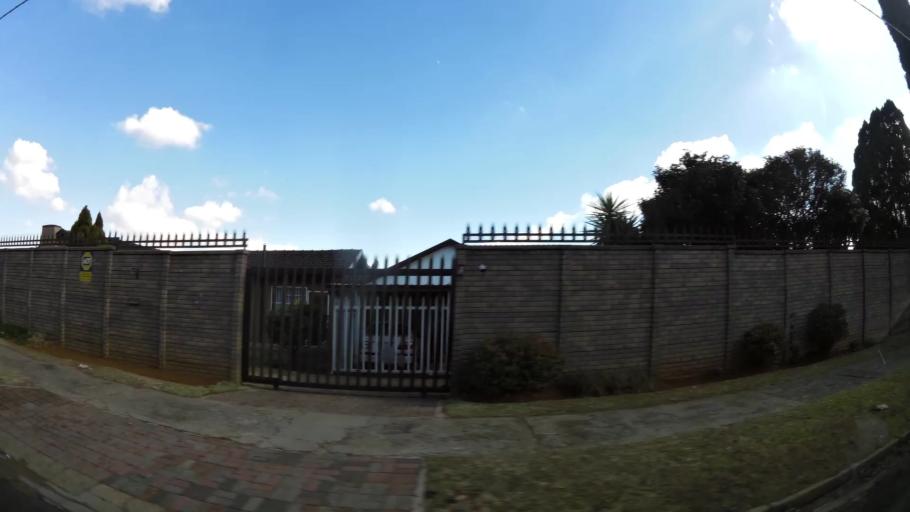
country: ZA
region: Gauteng
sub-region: City of Johannesburg Metropolitan Municipality
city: Roodepoort
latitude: -26.1360
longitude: 27.8301
